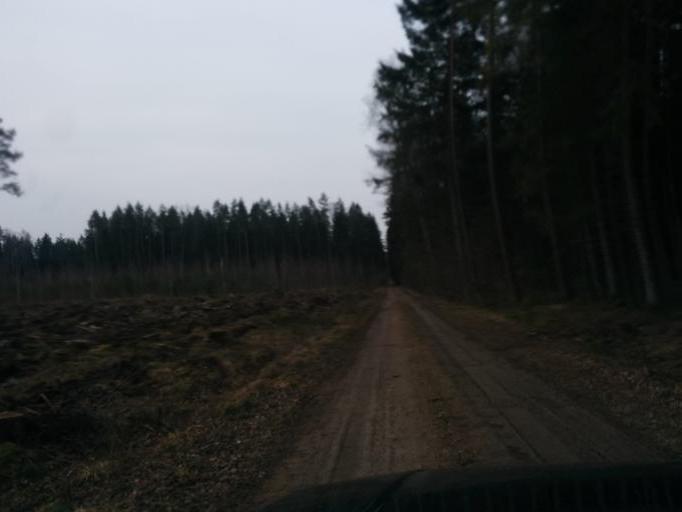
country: LV
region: Ikskile
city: Ikskile
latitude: 56.8083
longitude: 24.4820
